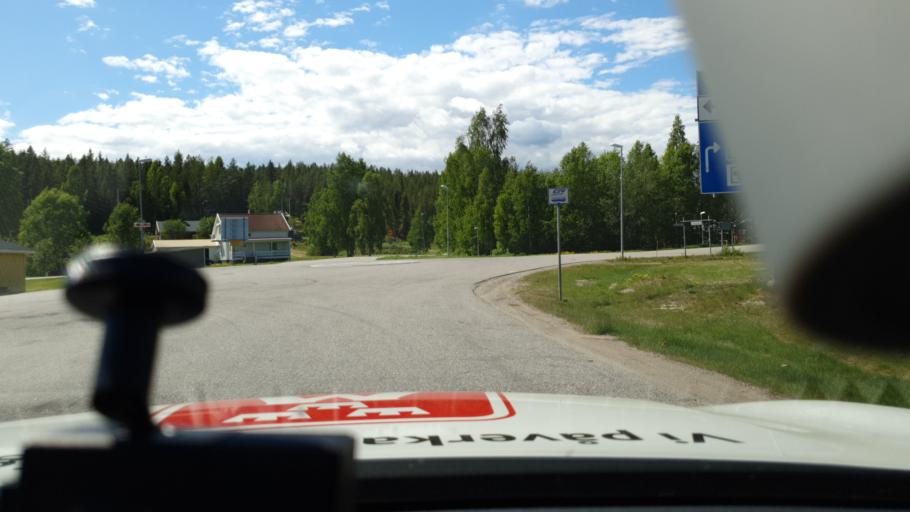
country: SE
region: Norrbotten
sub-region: Pitea Kommun
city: Pitea
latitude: 65.1437
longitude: 21.5035
